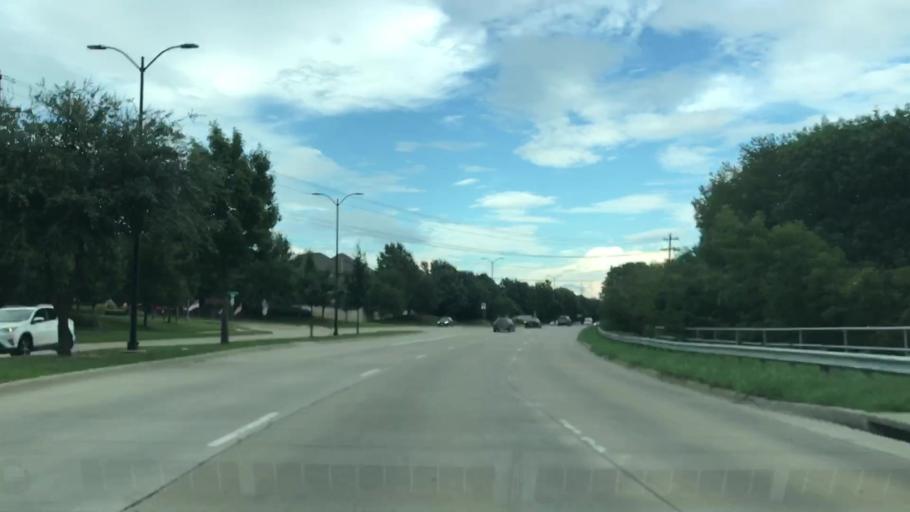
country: US
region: Texas
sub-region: Collin County
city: Frisco
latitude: 33.1752
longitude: -96.7992
